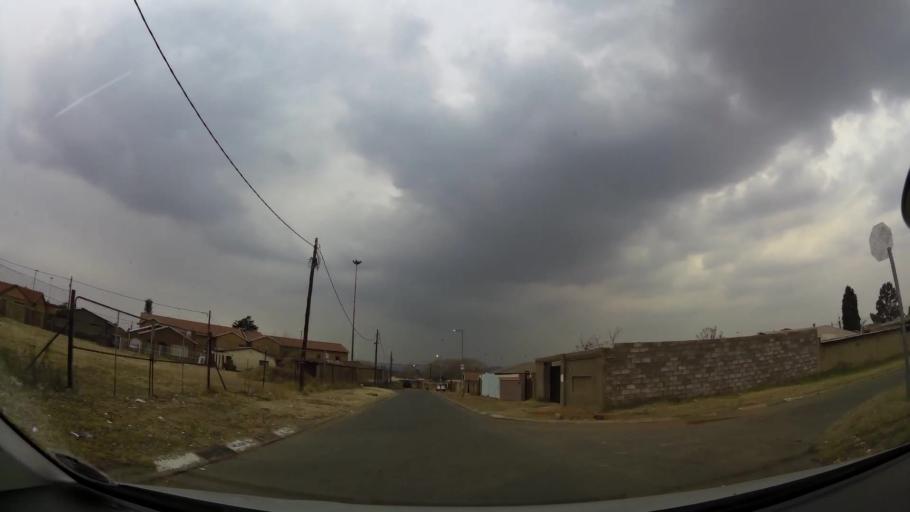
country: ZA
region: Gauteng
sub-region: City of Johannesburg Metropolitan Municipality
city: Soweto
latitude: -26.2623
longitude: 27.8670
